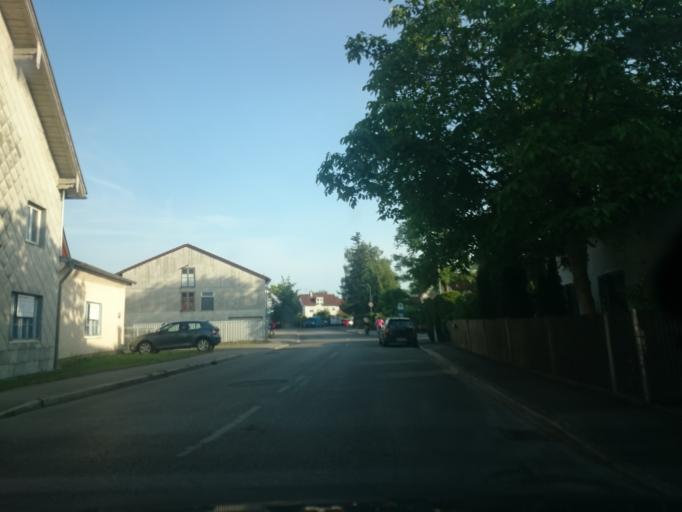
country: DE
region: Bavaria
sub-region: Upper Bavaria
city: Puchheim
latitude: 48.1272
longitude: 11.3486
